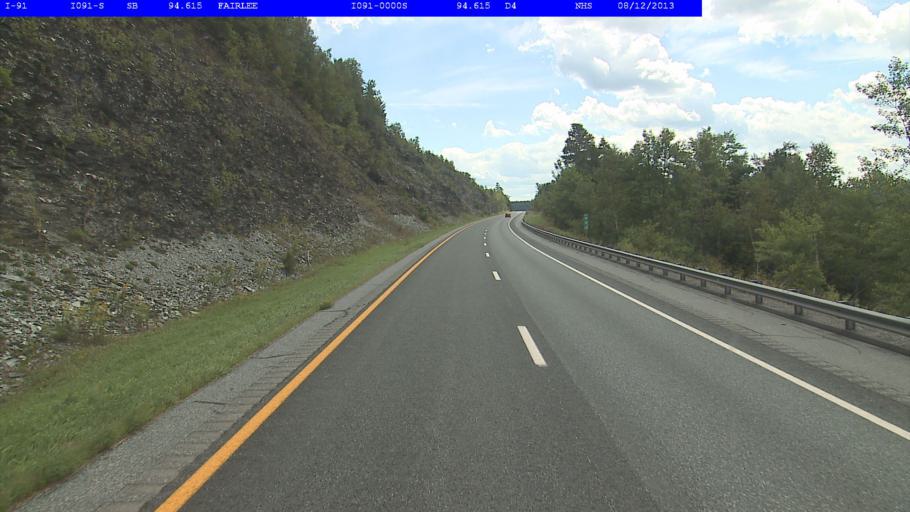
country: US
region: New Hampshire
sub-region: Grafton County
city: Orford
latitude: 43.9421
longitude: -72.1328
